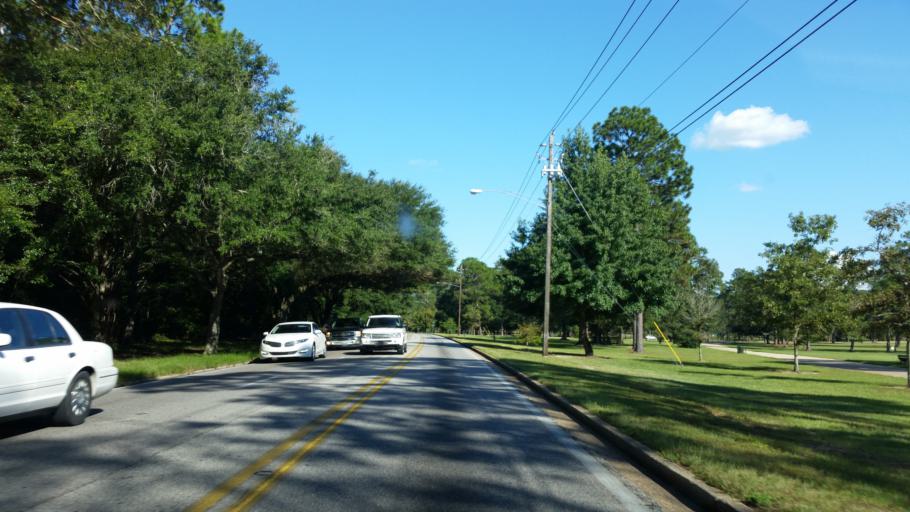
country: US
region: Alabama
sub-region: Mobile County
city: Prichard
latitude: 30.7101
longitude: -88.1607
